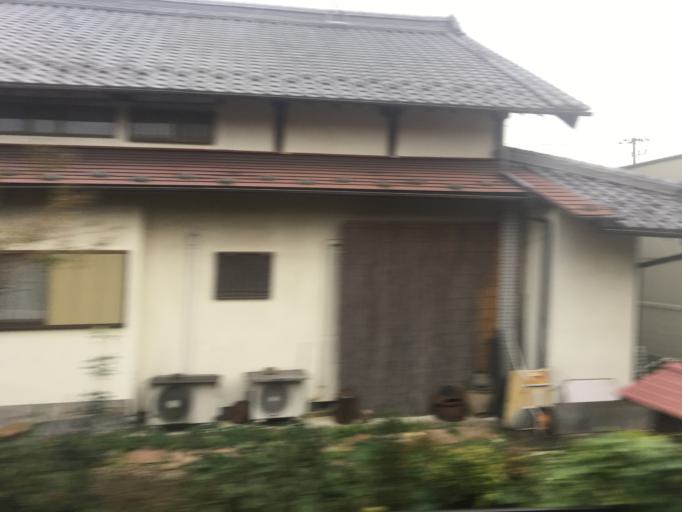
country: JP
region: Saitama
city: Sakado
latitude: 35.9081
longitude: 139.4085
